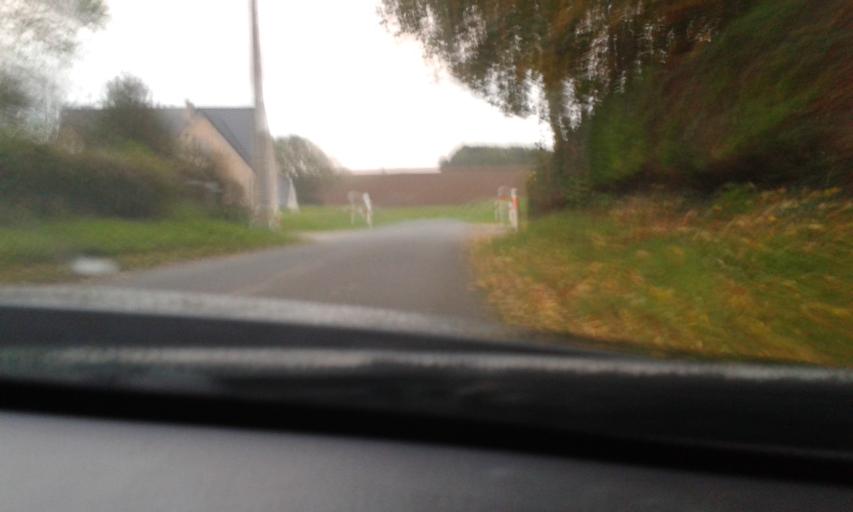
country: FR
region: Nord-Pas-de-Calais
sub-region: Departement du Pas-de-Calais
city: Hames-Boucres
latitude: 50.8699
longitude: 1.8049
